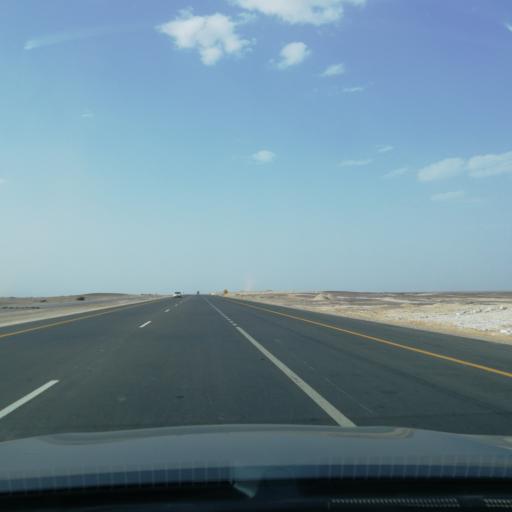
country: OM
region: Muhafazat ad Dakhiliyah
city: Adam
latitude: 22.0538
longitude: 57.5121
